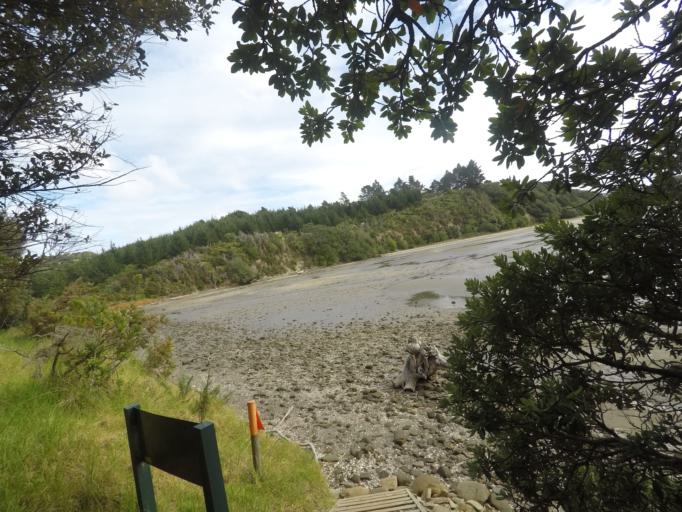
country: NZ
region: Auckland
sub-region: Auckland
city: Rothesay Bay
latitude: -36.6490
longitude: 174.7270
